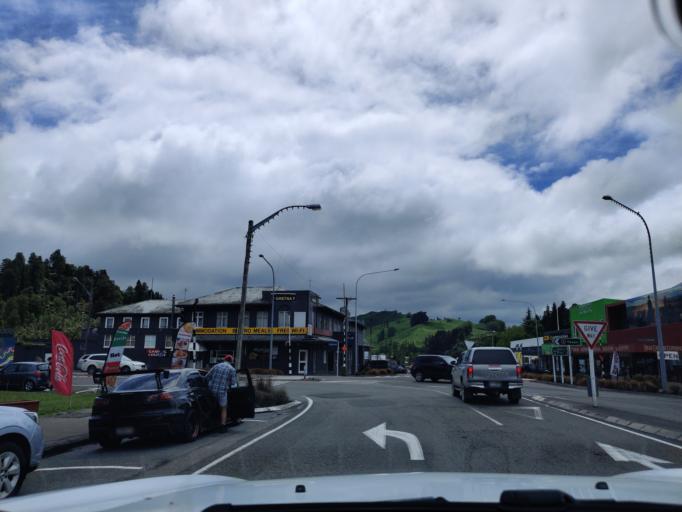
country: NZ
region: Manawatu-Wanganui
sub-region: Ruapehu District
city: Waiouru
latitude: -39.6765
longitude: 175.7982
